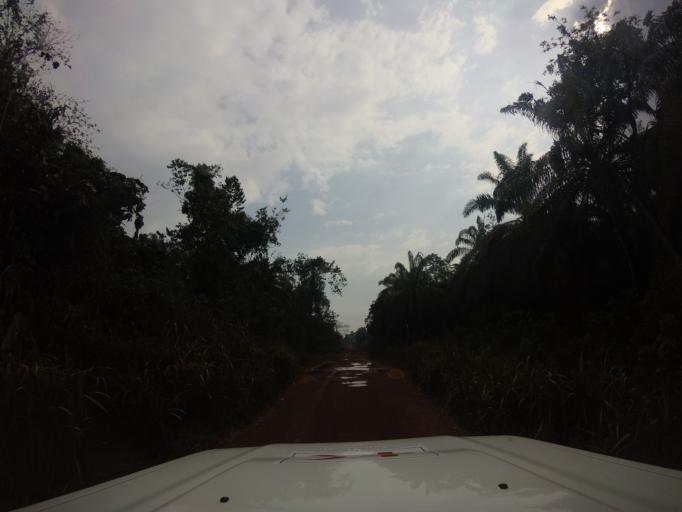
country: SL
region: Southern Province
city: Zimmi
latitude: 7.0488
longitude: -11.2808
